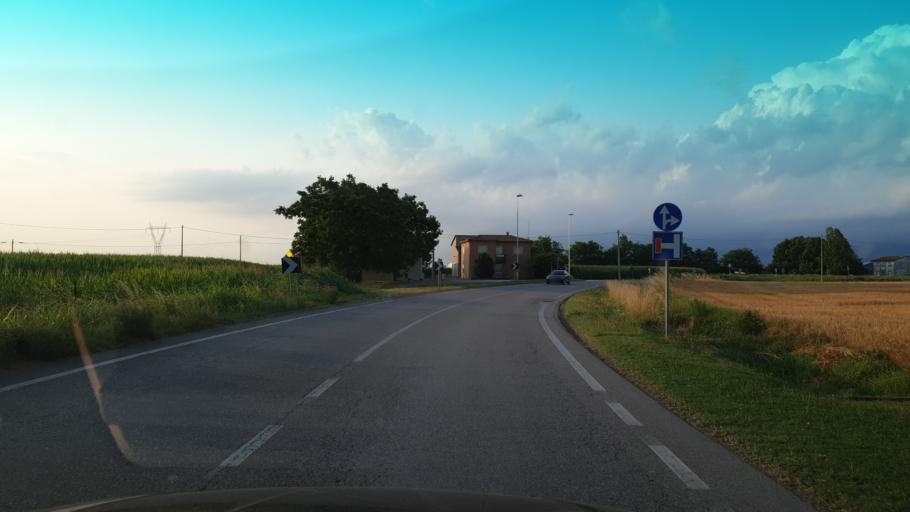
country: IT
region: Veneto
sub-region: Provincia di Rovigo
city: Lendinara
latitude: 45.0631
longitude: 11.5816
